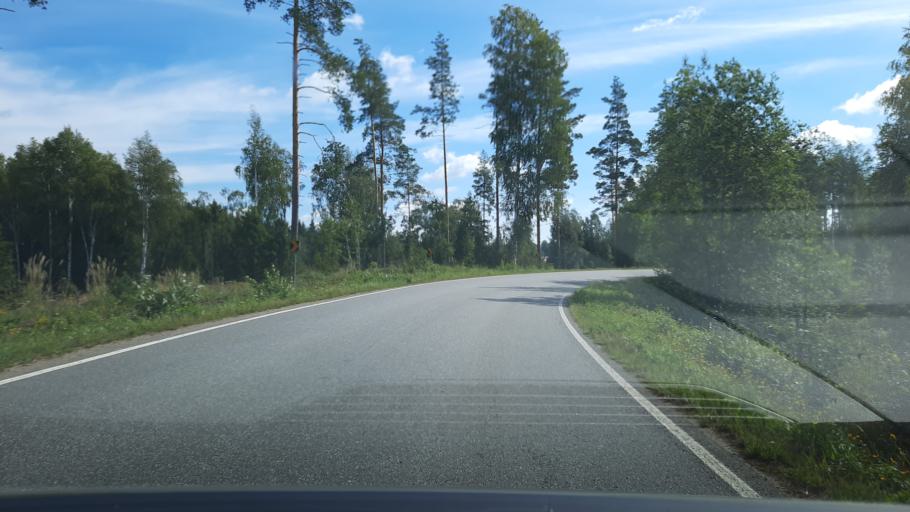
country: FI
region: Pirkanmaa
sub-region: Lounais-Pirkanmaa
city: Punkalaidun
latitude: 61.1903
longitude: 23.3162
